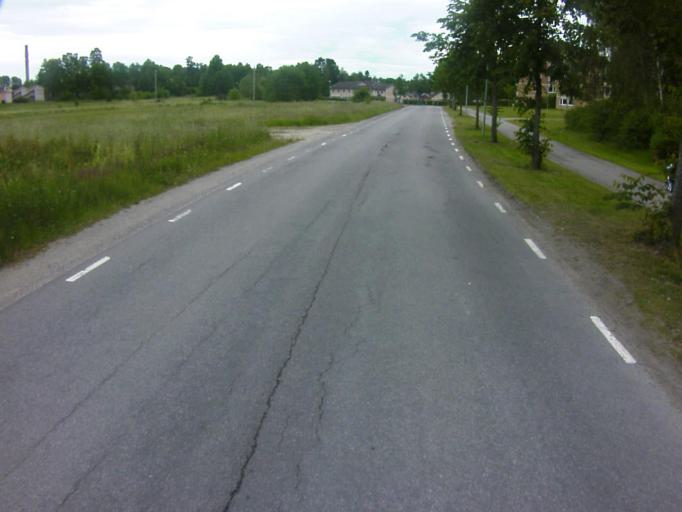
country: SE
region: Soedermanland
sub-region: Eskilstuna Kommun
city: Skogstorp
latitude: 59.3593
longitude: 16.4709
